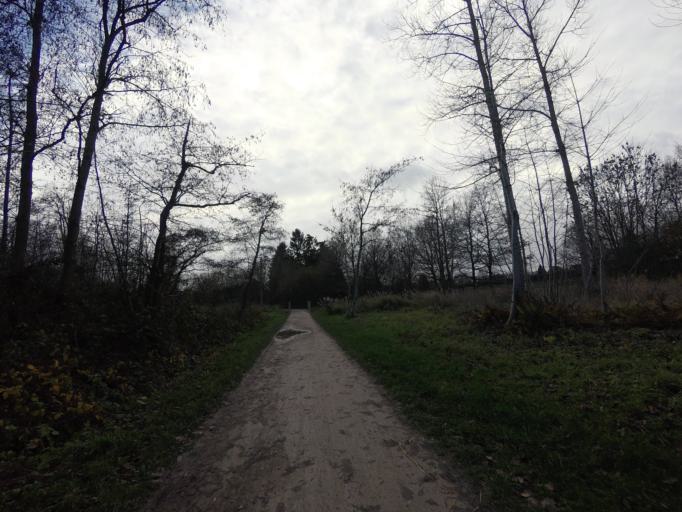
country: BE
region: Flanders
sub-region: Provincie Vlaams-Brabant
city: Haacht
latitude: 50.9635
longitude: 4.6316
